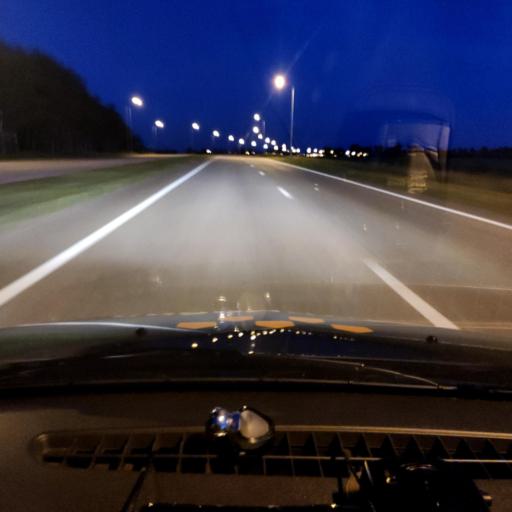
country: RU
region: Belgorod
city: Skorodnoye
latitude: 51.0861
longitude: 37.2142
